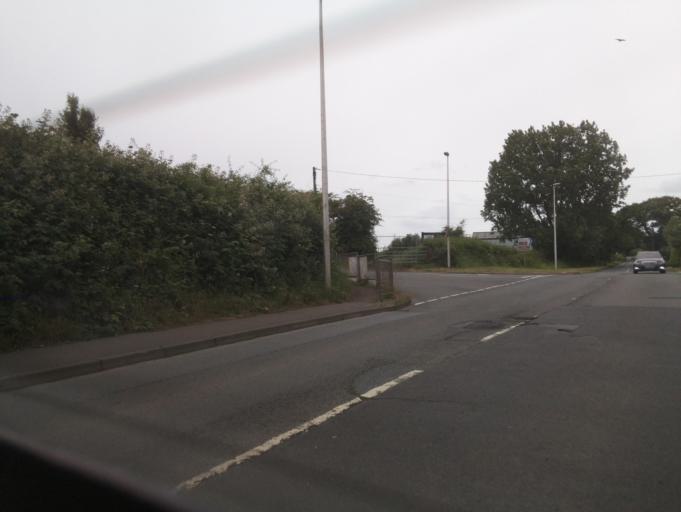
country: GB
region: England
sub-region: Devon
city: Ottery St Mary
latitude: 50.7494
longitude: -3.2932
